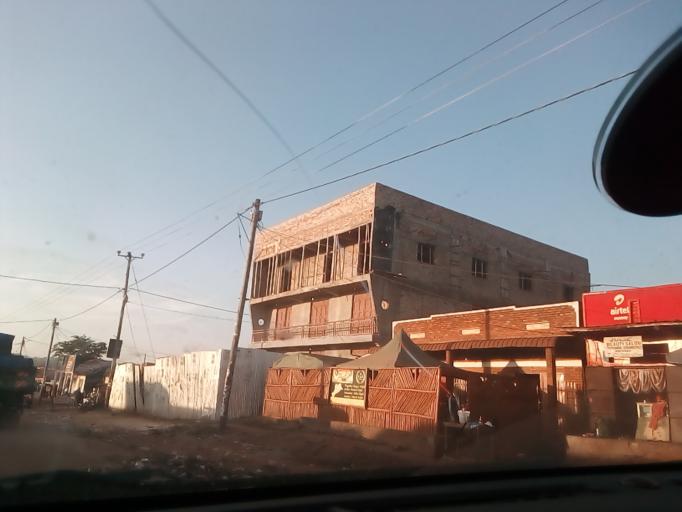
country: UG
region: Central Region
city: Masaka
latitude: -0.3223
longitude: 31.7611
